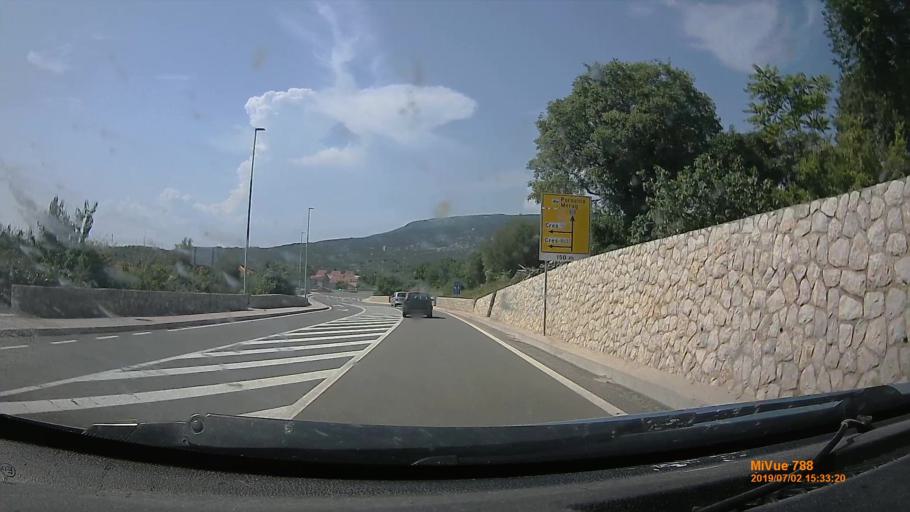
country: HR
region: Primorsko-Goranska
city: Cres
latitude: 44.9587
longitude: 14.4149
